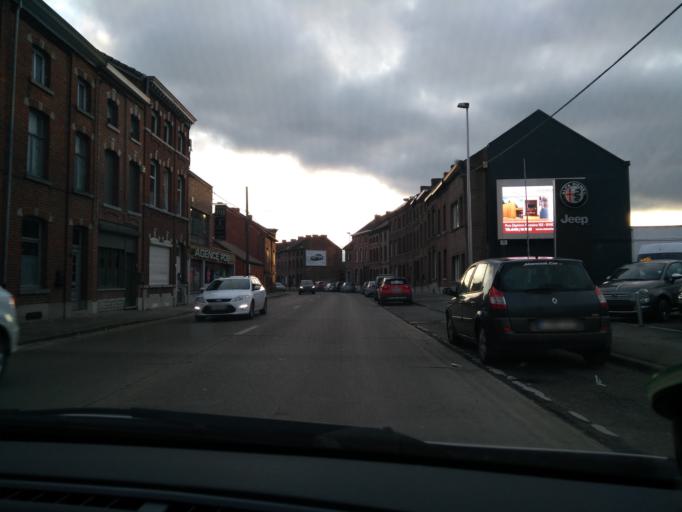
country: BE
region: Wallonia
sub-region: Province du Hainaut
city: Binche
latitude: 50.4187
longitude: 4.1697
